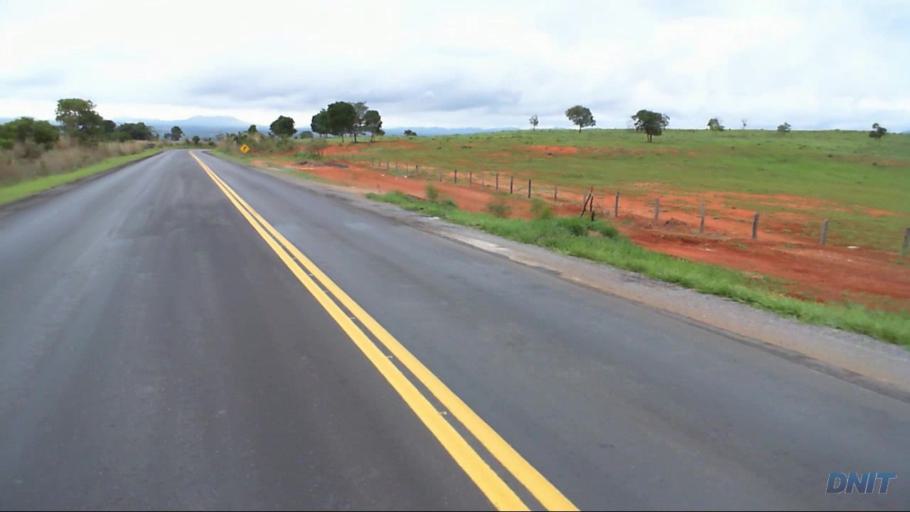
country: BR
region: Goias
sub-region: Padre Bernardo
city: Padre Bernardo
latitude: -15.2209
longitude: -48.5219
